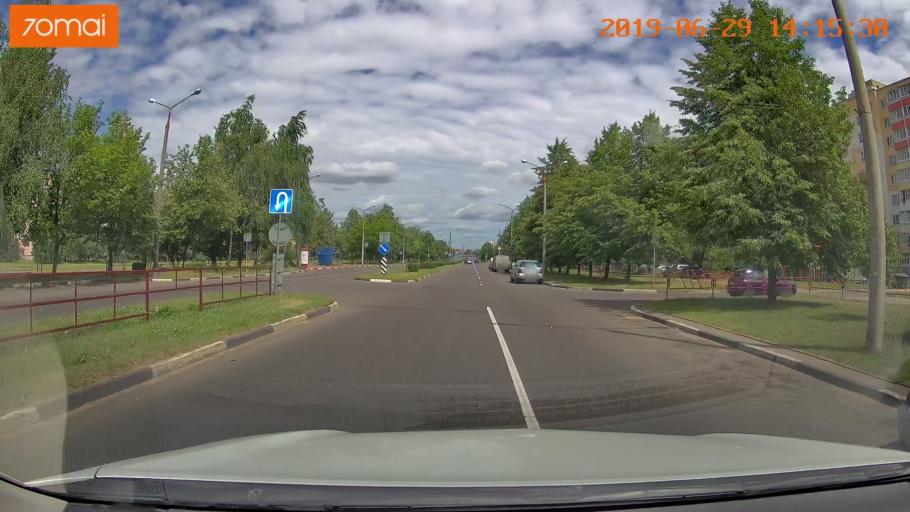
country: BY
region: Minsk
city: Salihorsk
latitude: 52.7919
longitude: 27.5204
